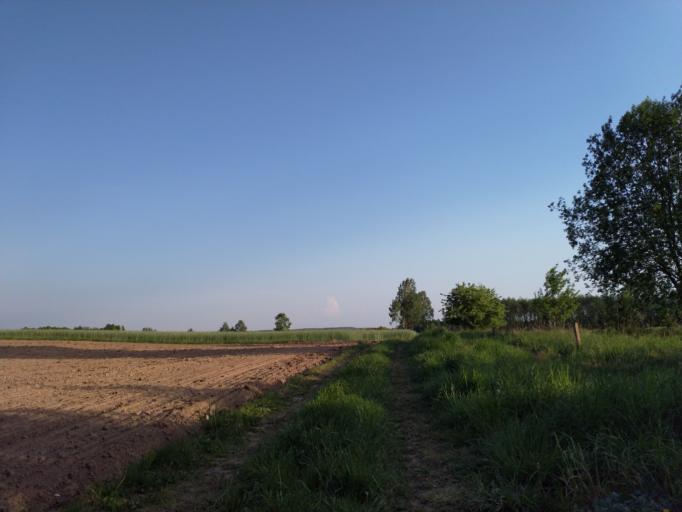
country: LV
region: Aizpute
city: Aizpute
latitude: 56.8313
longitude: 21.7825
